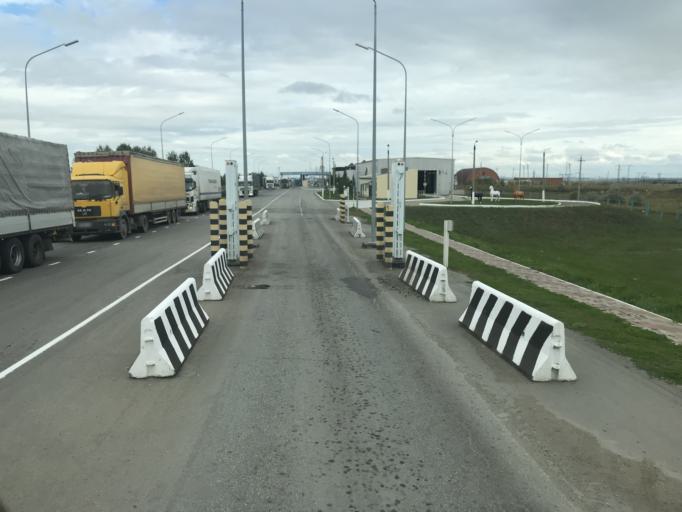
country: RU
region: Chelyabinsk
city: Bobrovka
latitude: 53.9988
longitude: 61.6415
